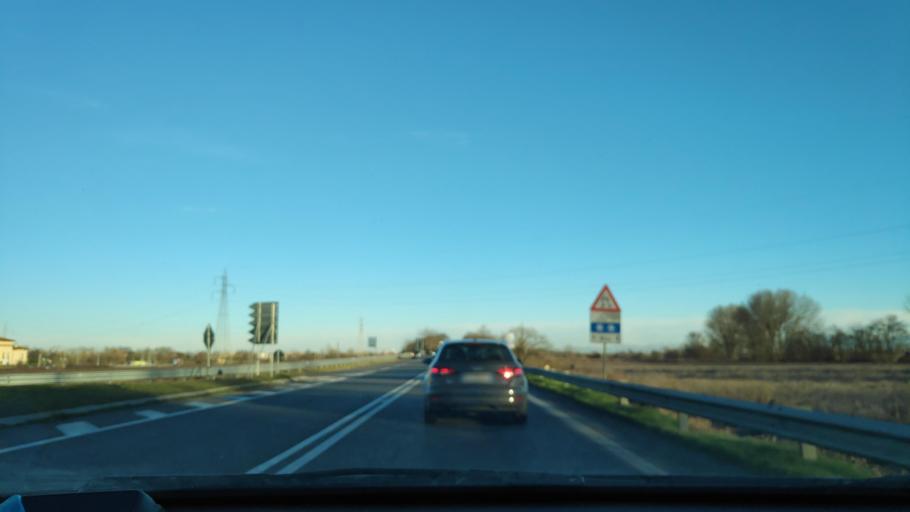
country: IT
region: Lombardy
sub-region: Citta metropolitana di Milano
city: Locate di Triulzi
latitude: 45.3619
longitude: 9.2310
